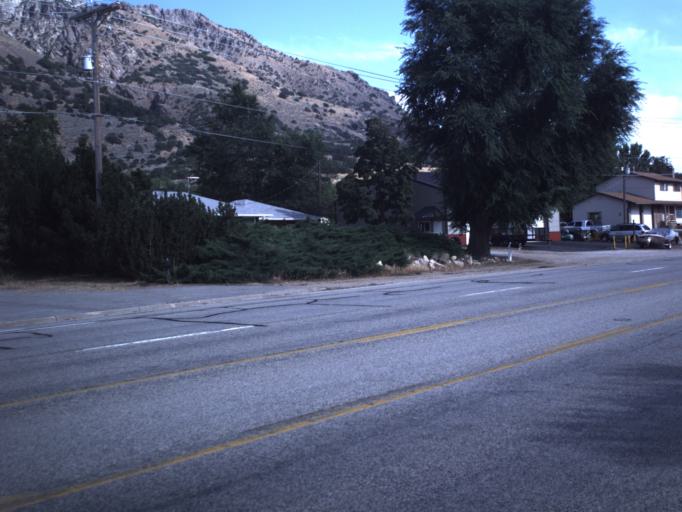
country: US
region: Utah
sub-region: Box Elder County
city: Willard
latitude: 41.3968
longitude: -112.0344
